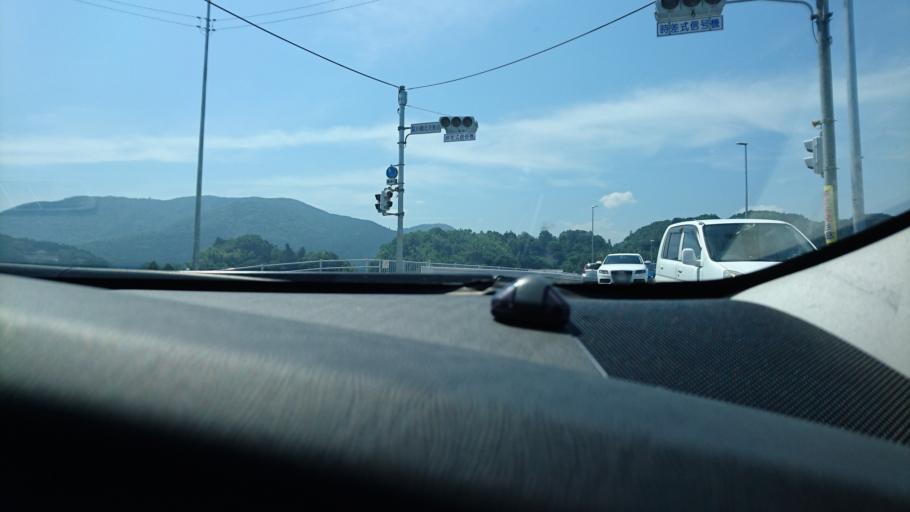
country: JP
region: Ehime
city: Ozu
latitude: 33.5099
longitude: 132.5456
